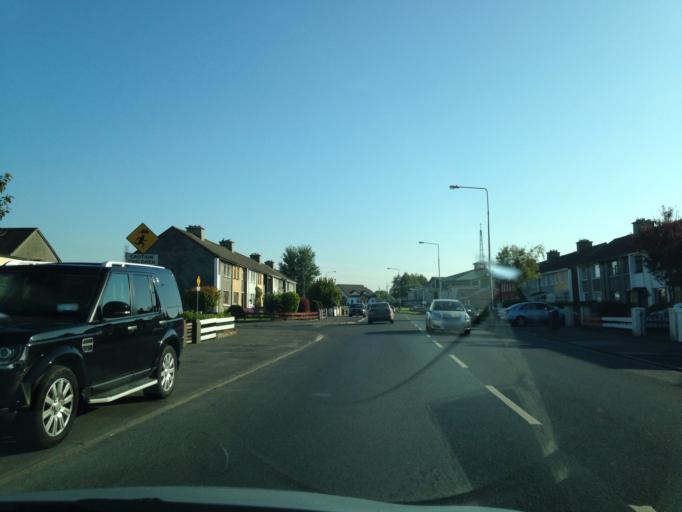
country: IE
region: Connaught
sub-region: County Galway
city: Gaillimh
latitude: 53.2801
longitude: -9.0173
